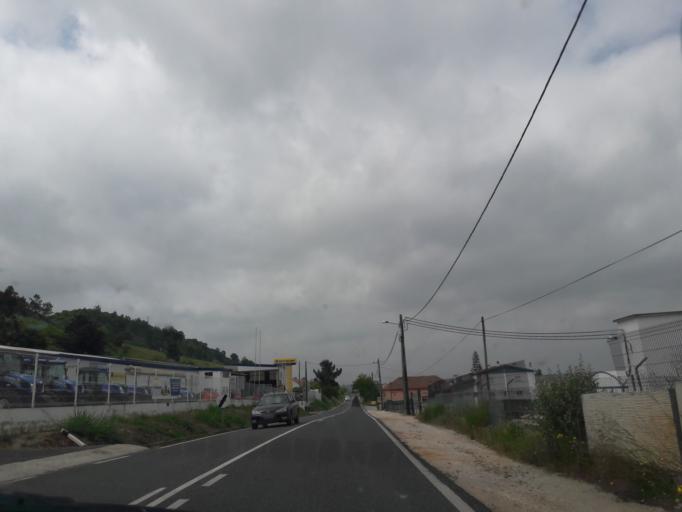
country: PT
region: Leiria
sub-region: Obidos
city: Obidos
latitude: 39.3466
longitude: -9.1632
